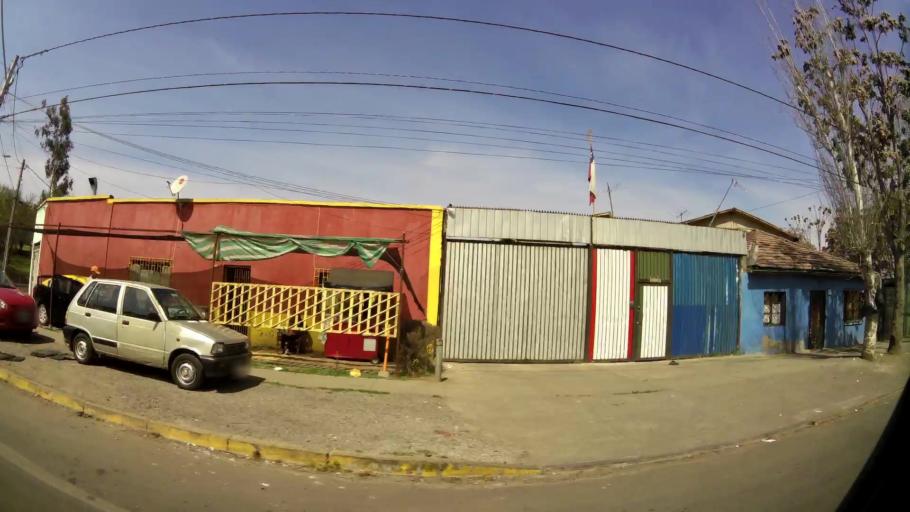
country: CL
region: Santiago Metropolitan
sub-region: Provincia de Santiago
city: Lo Prado
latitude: -33.4240
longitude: -70.7221
